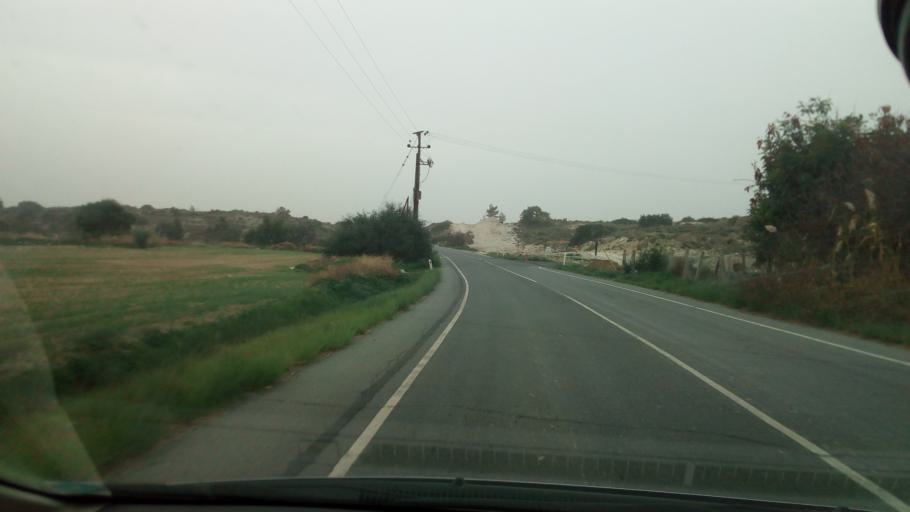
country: CY
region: Larnaka
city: Kofinou
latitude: 34.7631
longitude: 33.3227
